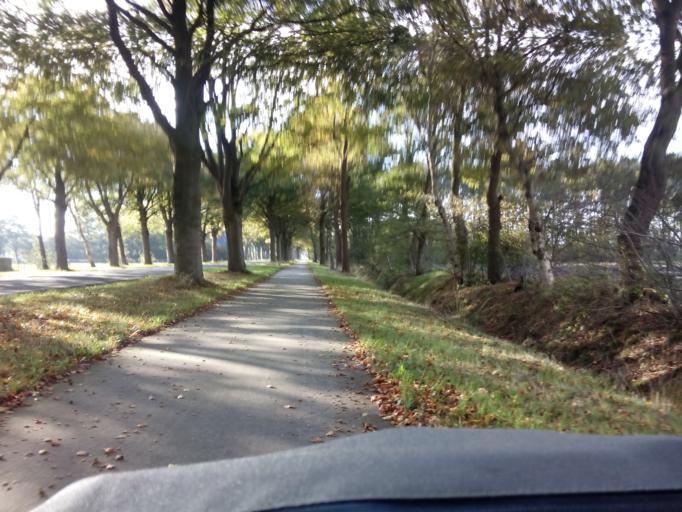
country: NL
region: Drenthe
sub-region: Gemeente Tynaarlo
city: Vries
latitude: 53.0495
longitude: 6.5738
